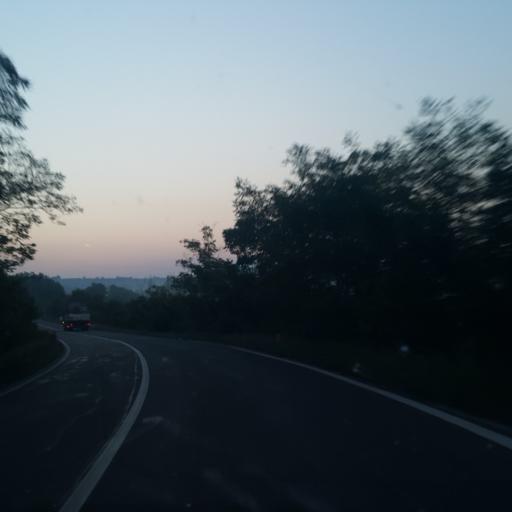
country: RS
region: Central Serbia
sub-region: Nisavski Okrug
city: Svrljig
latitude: 43.4288
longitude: 22.1424
